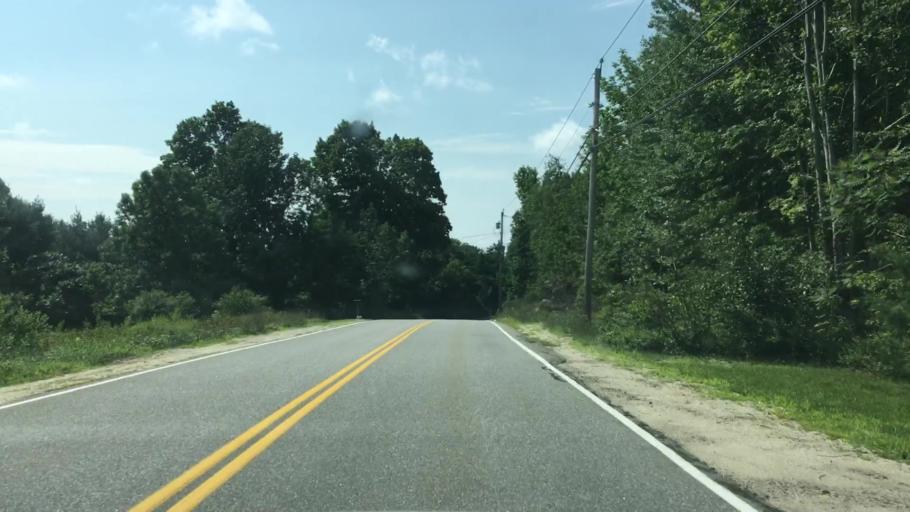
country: US
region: Maine
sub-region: Cumberland County
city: Raymond
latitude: 43.9416
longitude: -70.4383
